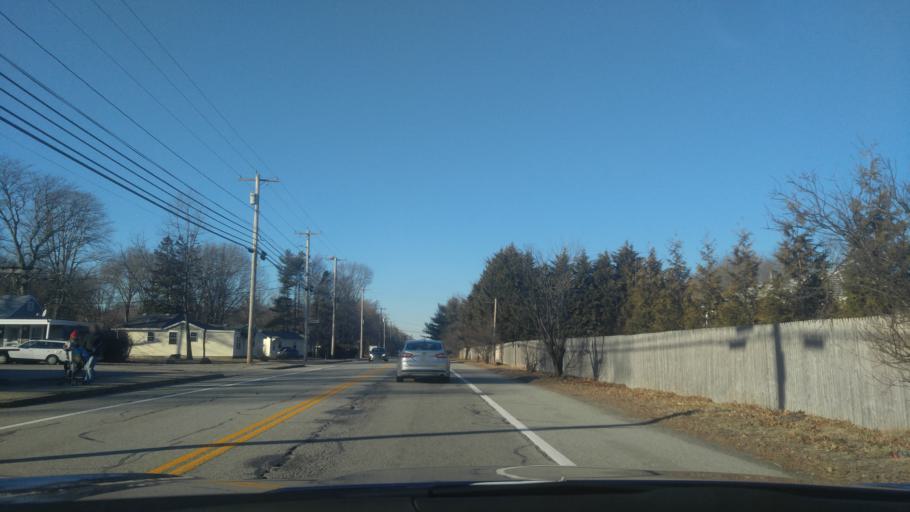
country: US
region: Rhode Island
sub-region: Washington County
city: Narragansett Pier
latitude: 41.4837
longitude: -71.4369
